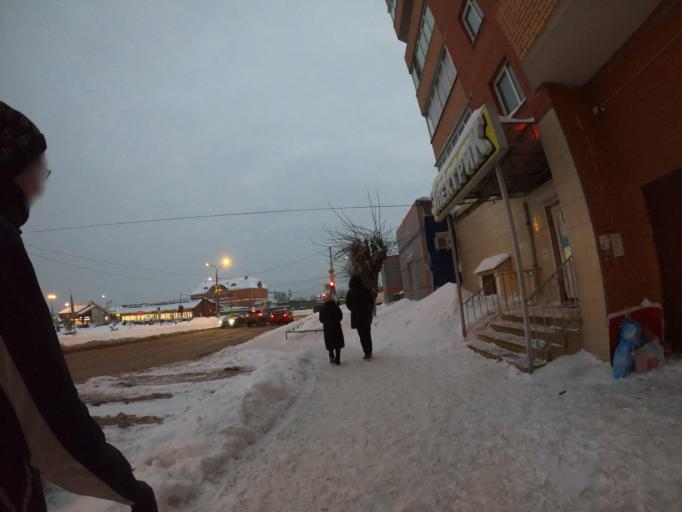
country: RU
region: Moskovskaya
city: Pavlovskiy Posad
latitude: 55.7771
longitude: 38.6718
